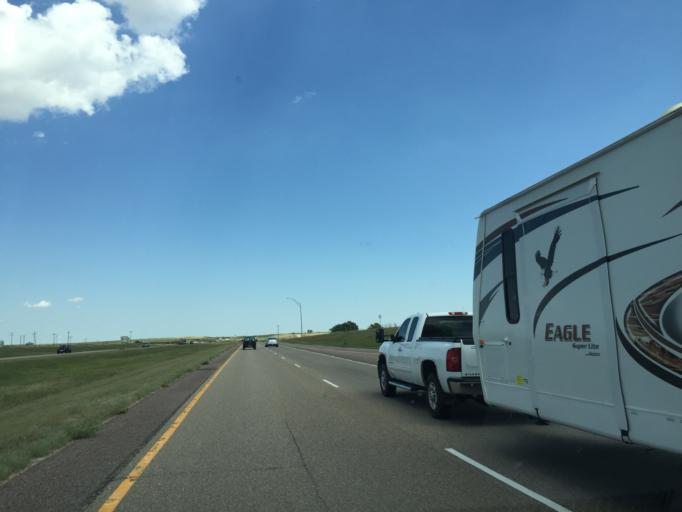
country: US
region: Colorado
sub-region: Lincoln County
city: Hugo
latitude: 39.2789
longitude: -103.3944
